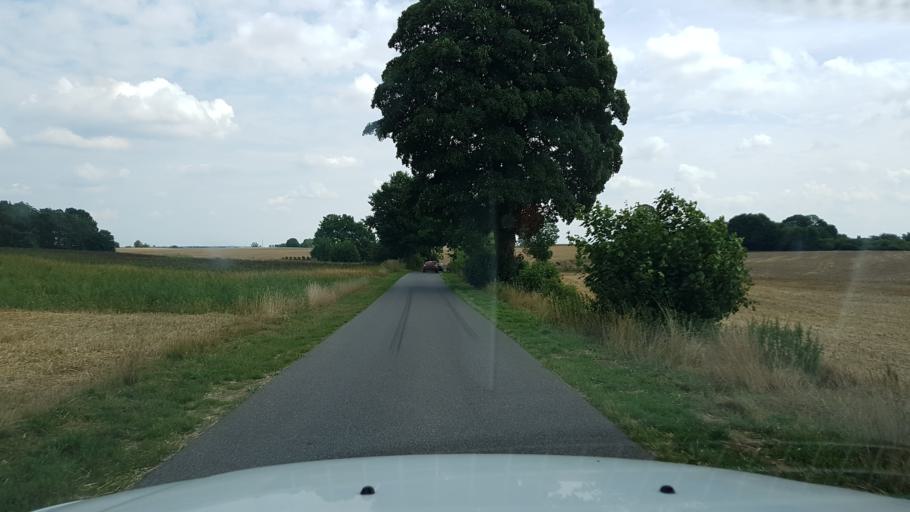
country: PL
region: West Pomeranian Voivodeship
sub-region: Powiat walecki
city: Walcz
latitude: 53.2299
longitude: 16.5065
